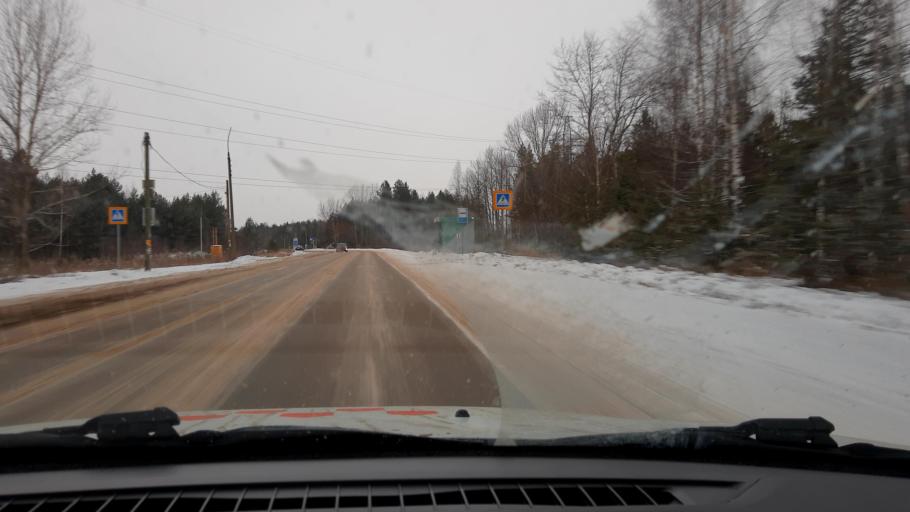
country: RU
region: Nizjnij Novgorod
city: Bor
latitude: 56.3234
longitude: 44.1459
